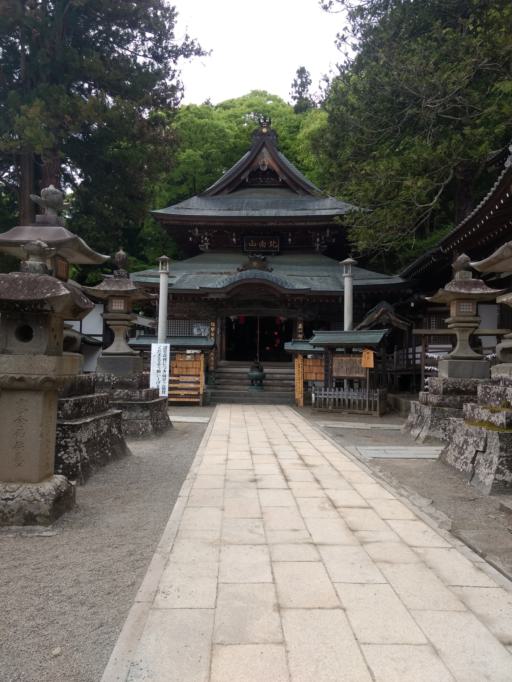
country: JP
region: Nagano
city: Kamimaruko
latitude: 36.3501
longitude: 138.1563
